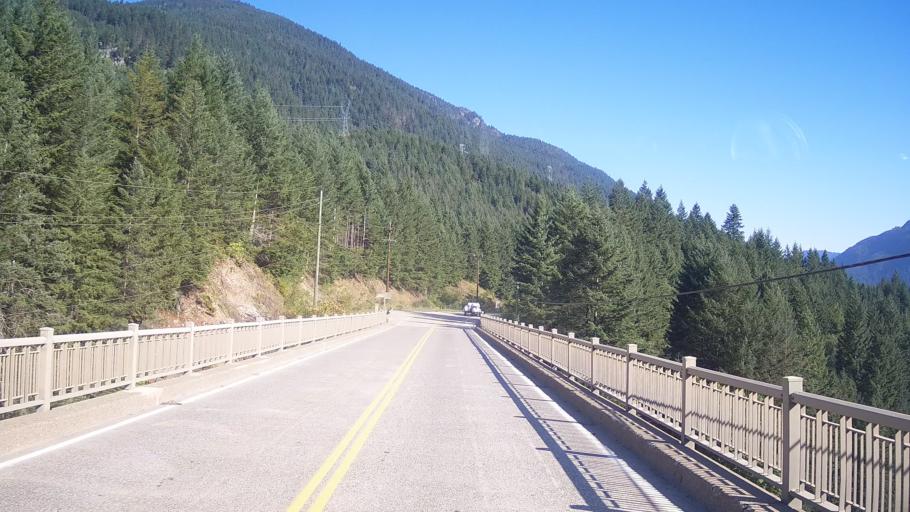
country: CA
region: British Columbia
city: Hope
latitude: 49.6651
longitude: -121.4194
